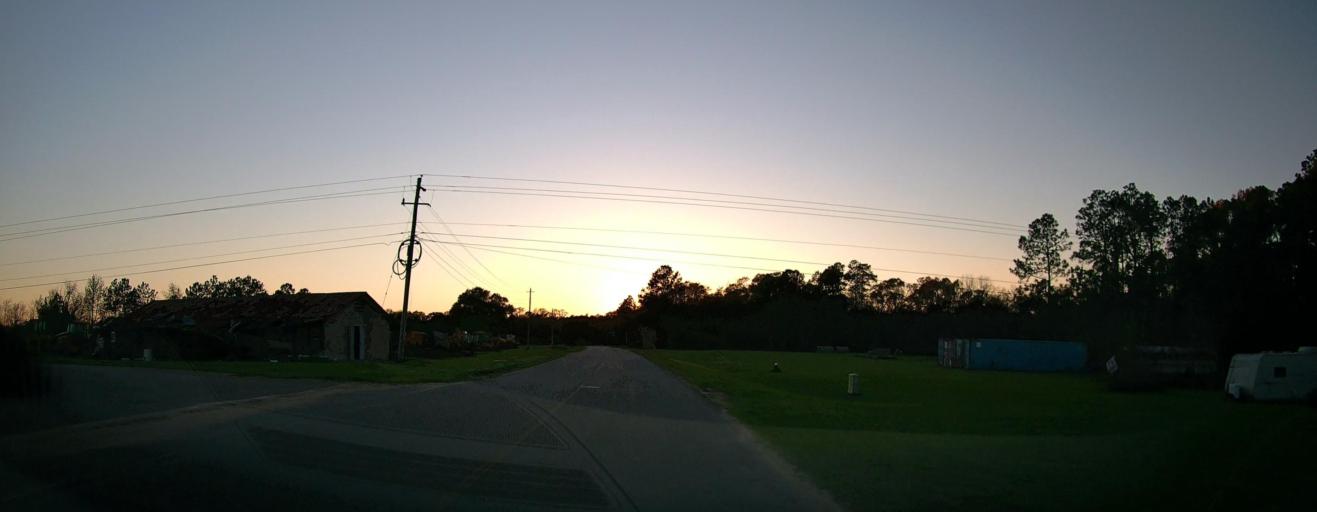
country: US
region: Georgia
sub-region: Crisp County
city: Cordele
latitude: 31.9288
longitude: -83.7785
